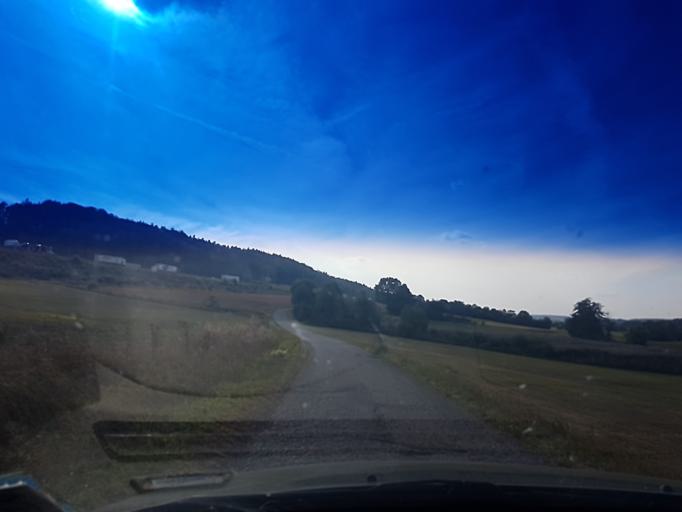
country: DE
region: Bavaria
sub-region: Regierungsbezirk Mittelfranken
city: Burghaslach
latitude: 49.7637
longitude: 10.5535
